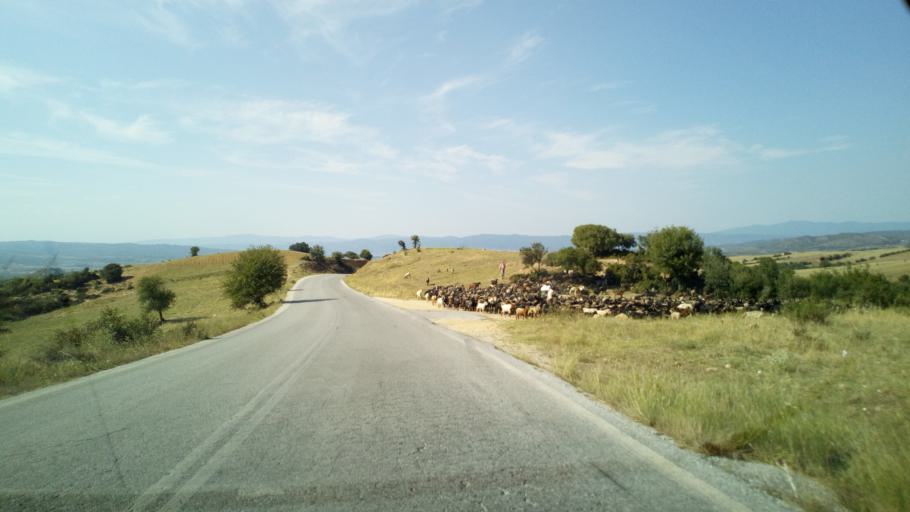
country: GR
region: Central Macedonia
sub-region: Nomos Thessalonikis
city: Nea Apollonia
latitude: 40.5163
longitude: 23.4732
